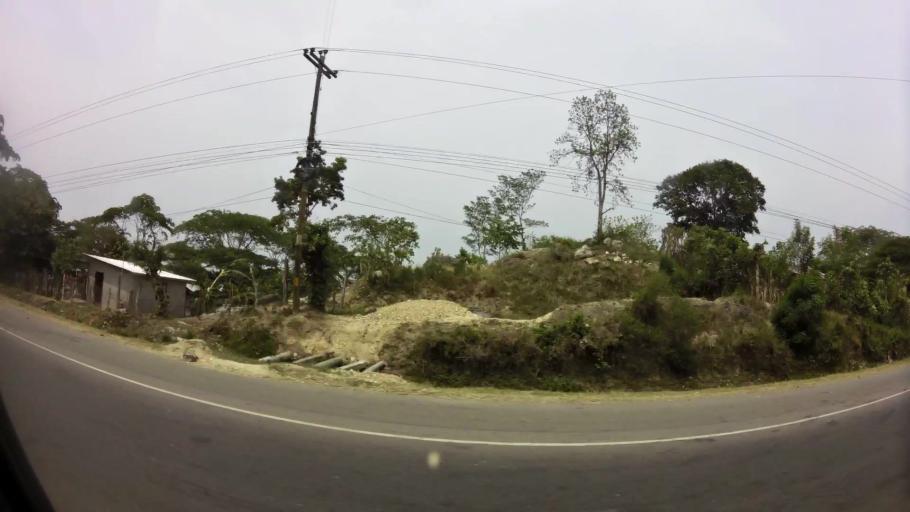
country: HN
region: Cortes
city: Nuevo Chamelecon
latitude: 15.3791
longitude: -87.9890
